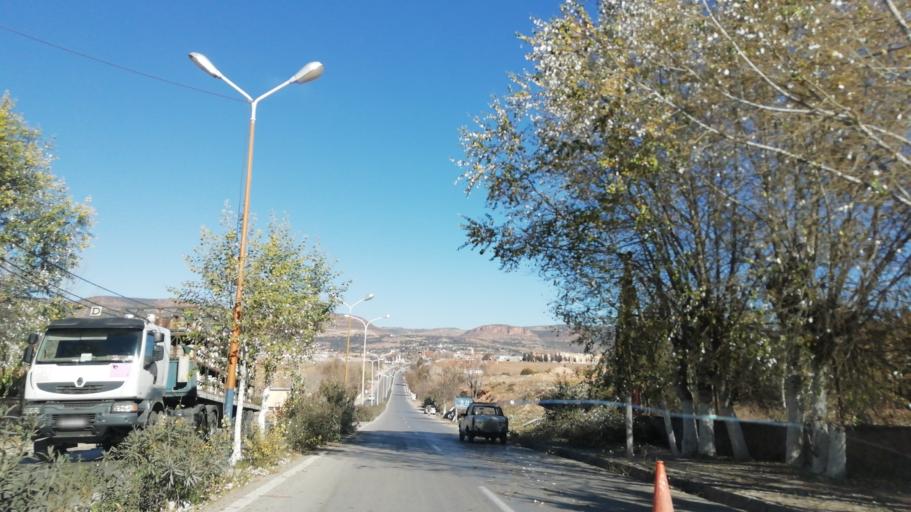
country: DZ
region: Tlemcen
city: Sebdou
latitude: 34.6539
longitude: -1.3255
